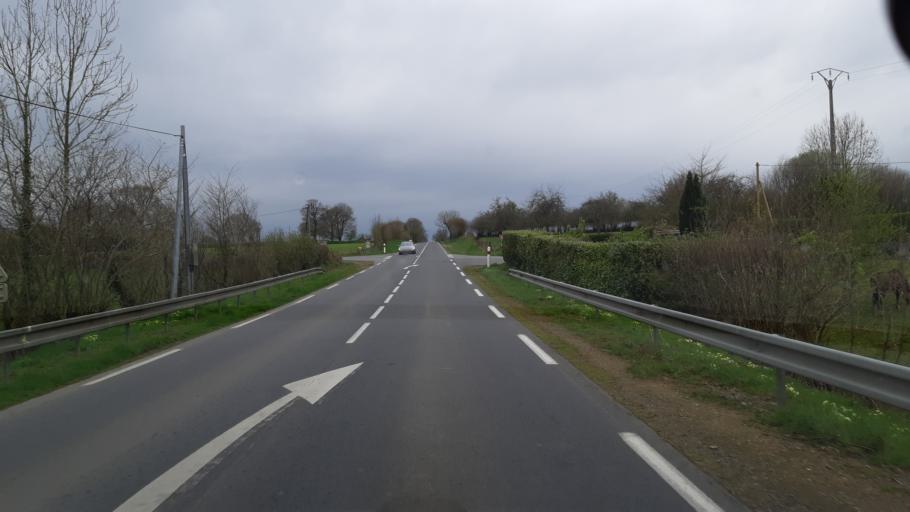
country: FR
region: Lower Normandy
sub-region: Departement de la Manche
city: Hambye
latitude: 48.9519
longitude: -1.2362
